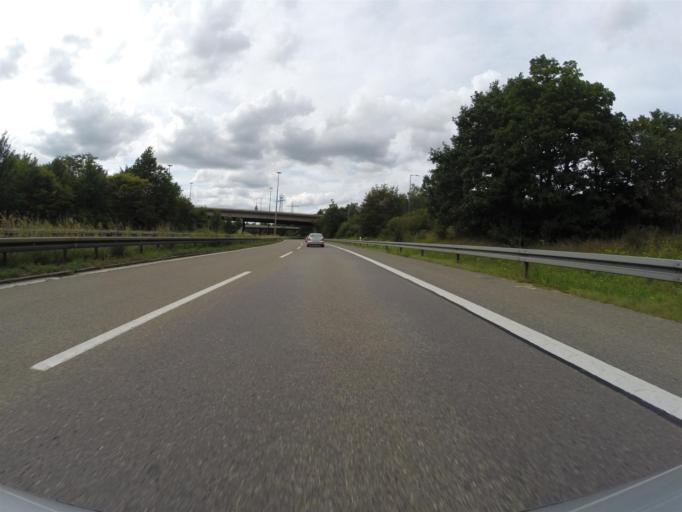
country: DE
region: Bavaria
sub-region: Regierungsbezirk Mittelfranken
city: Nuernberg
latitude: 49.4127
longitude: 11.0670
